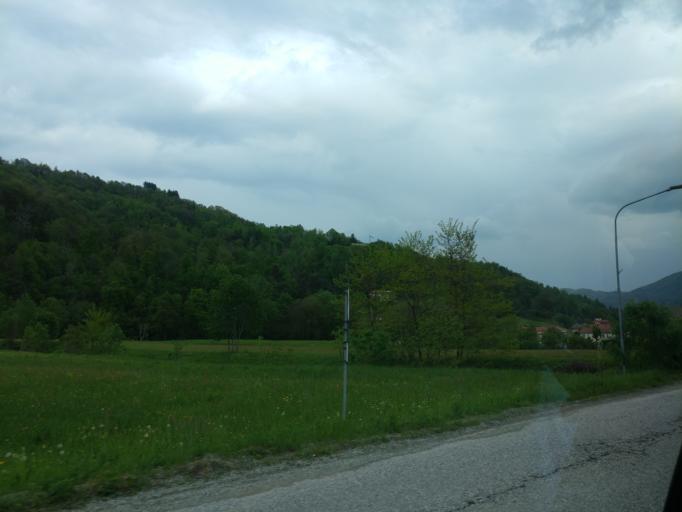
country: IT
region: Piedmont
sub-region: Provincia di Cuneo
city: Paesana
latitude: 44.6852
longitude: 7.2600
